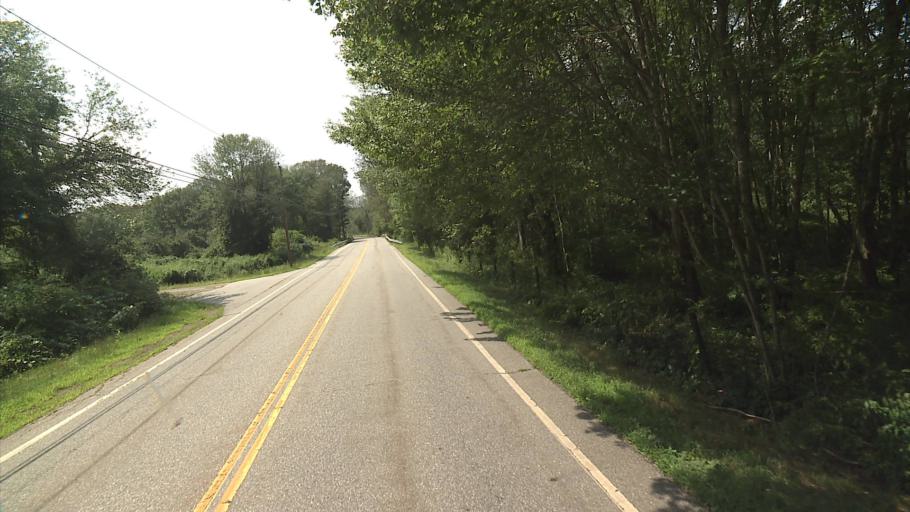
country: US
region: Connecticut
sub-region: Middlesex County
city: Essex Village
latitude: 41.4420
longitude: -72.3313
